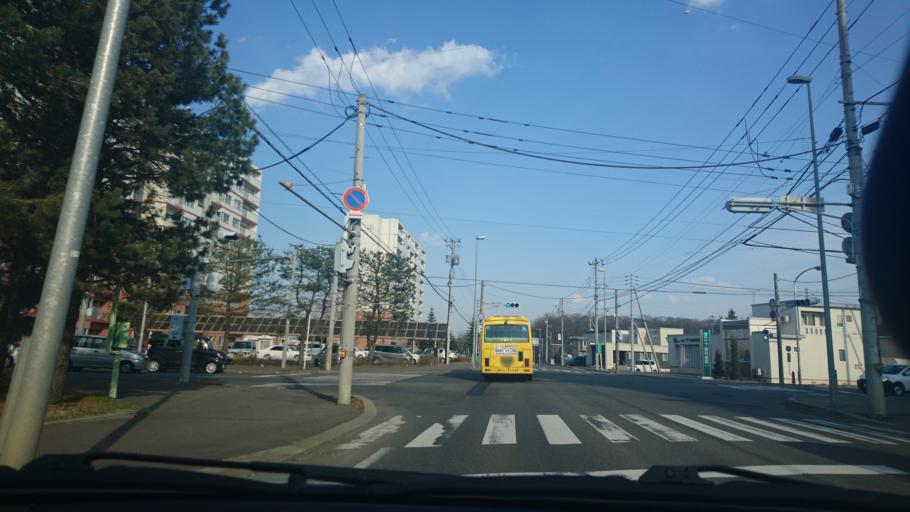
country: JP
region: Hokkaido
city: Obihiro
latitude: 42.9249
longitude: 143.1706
